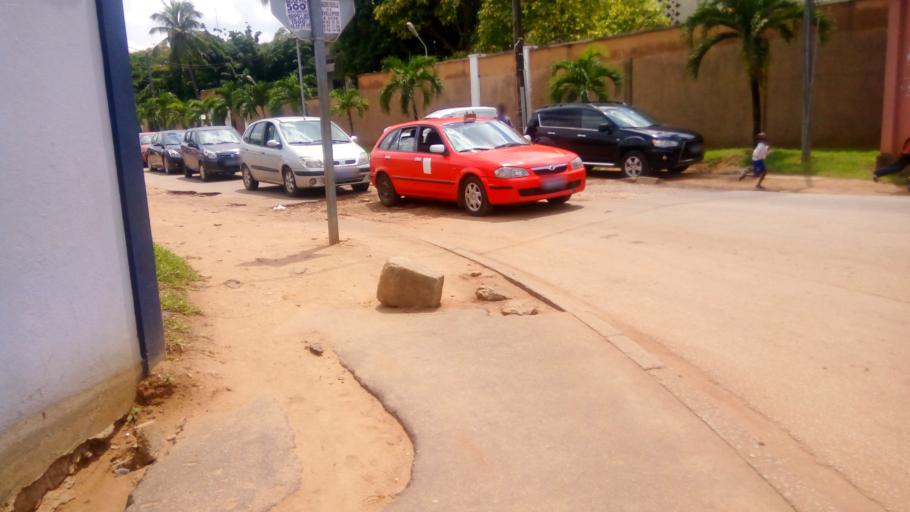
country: CI
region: Lagunes
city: Abidjan
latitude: 5.3381
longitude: -4.0218
